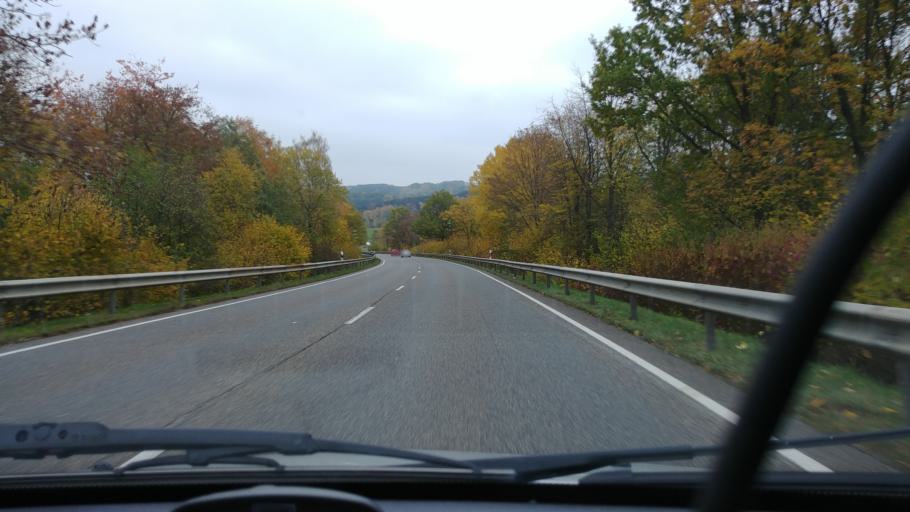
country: DE
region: Rheinland-Pfalz
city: Hachenburg
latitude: 50.6696
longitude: 7.8131
